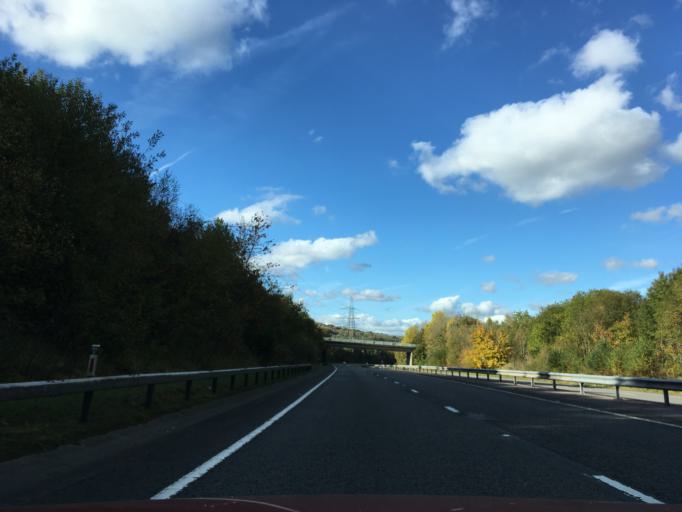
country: GB
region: Wales
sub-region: Merthyr Tydfil County Borough
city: Abercanaid
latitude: 51.7236
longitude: -3.3712
